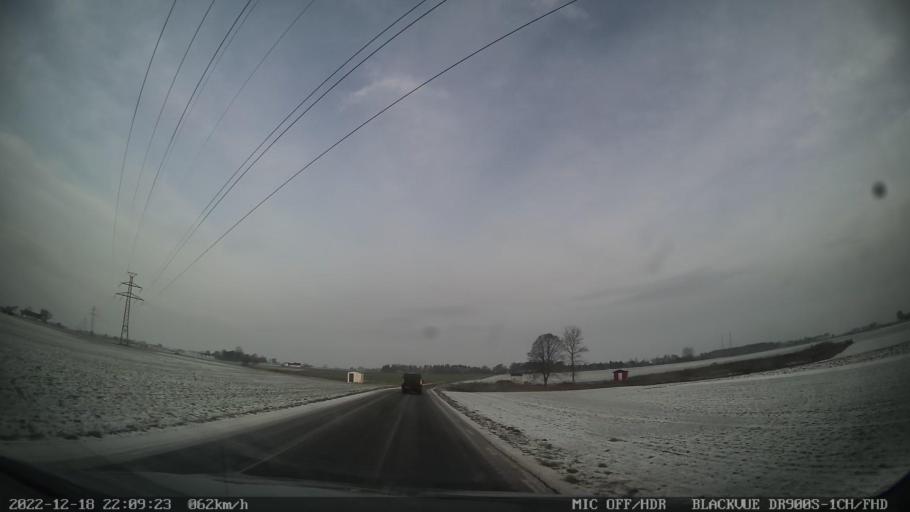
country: SE
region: Skane
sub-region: Tomelilla Kommun
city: Tomelilla
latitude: 55.5331
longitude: 14.0415
